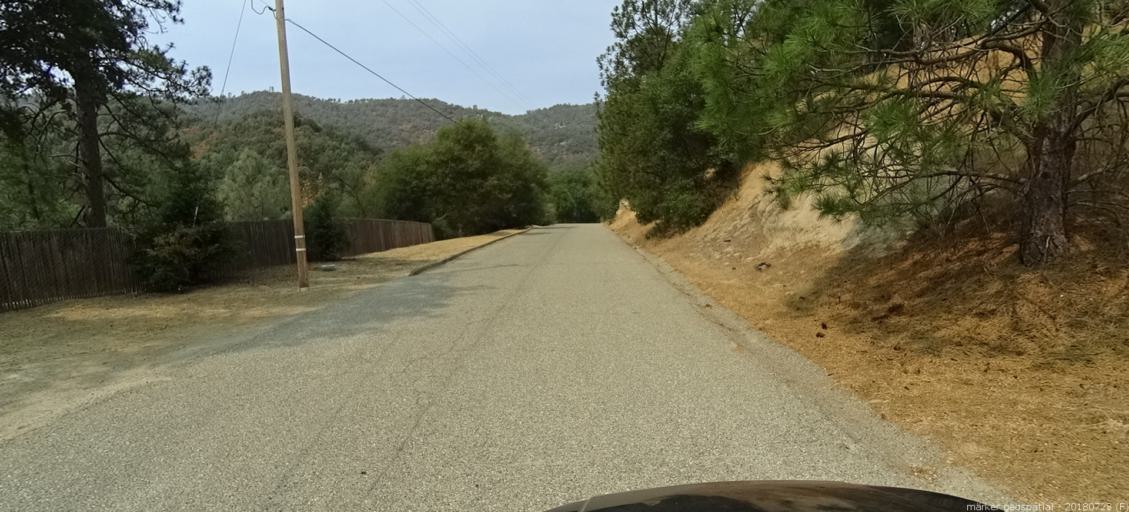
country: US
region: California
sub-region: Madera County
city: Ahwahnee
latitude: 37.3352
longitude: -119.7099
